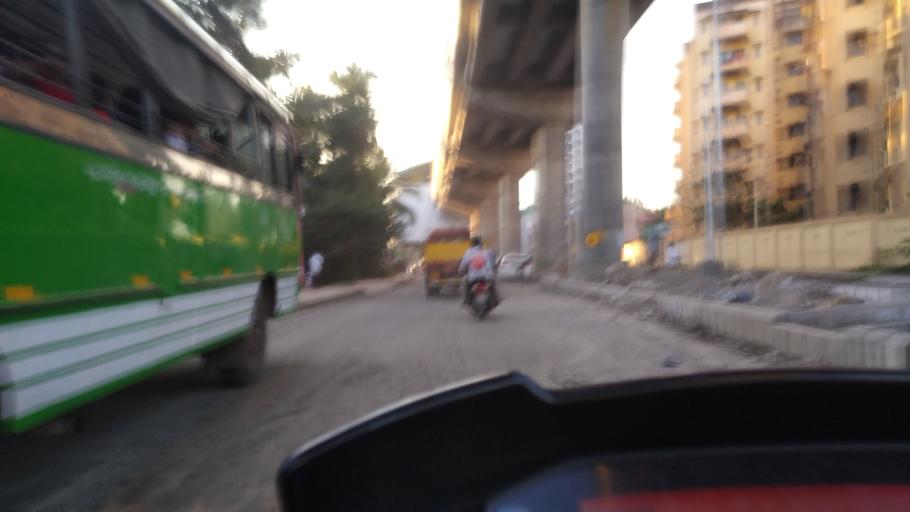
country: IN
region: Kerala
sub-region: Ernakulam
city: Cochin
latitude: 9.9583
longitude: 76.3257
